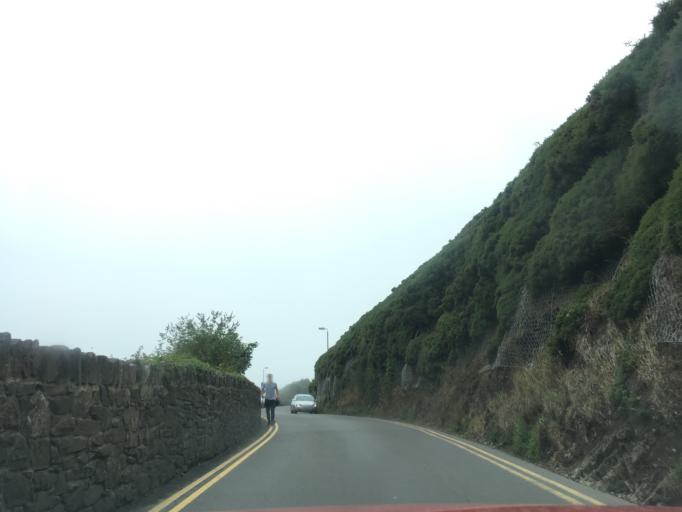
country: GB
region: Wales
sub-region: Pembrokeshire
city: Llanrhian
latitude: 51.8742
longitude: -5.1901
